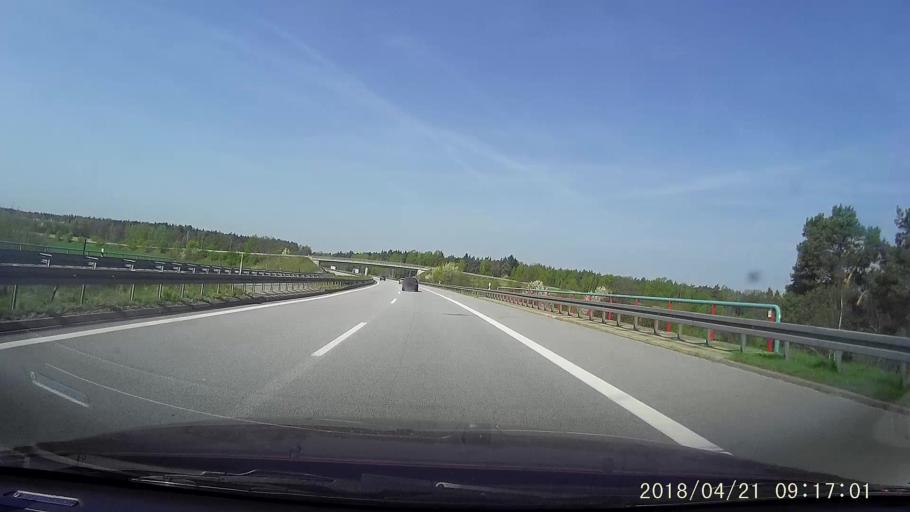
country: DE
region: Saxony
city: Weissenberg
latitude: 51.2137
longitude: 14.7197
